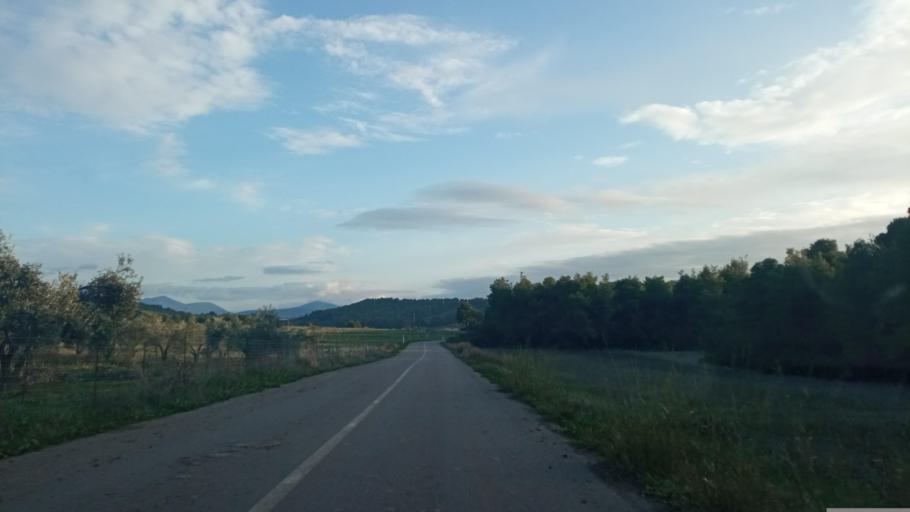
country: GR
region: Central Greece
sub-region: Nomos Evvoias
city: Kastella
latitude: 38.5595
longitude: 23.7121
